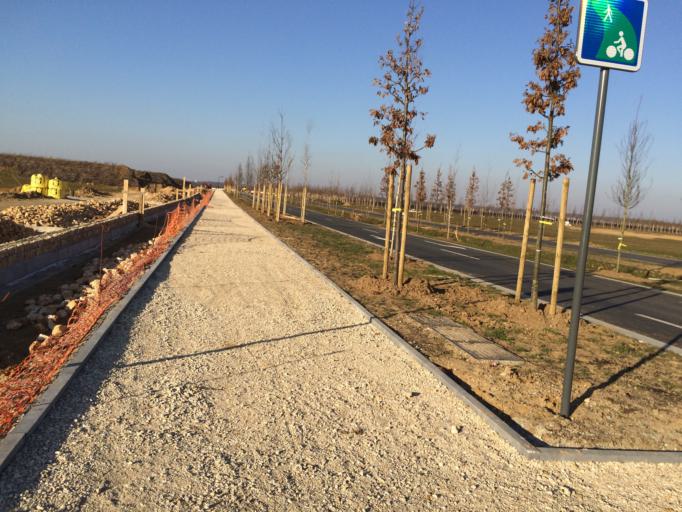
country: FR
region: Ile-de-France
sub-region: Departement de l'Essonne
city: Vauhallan
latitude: 48.7193
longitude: 2.1934
